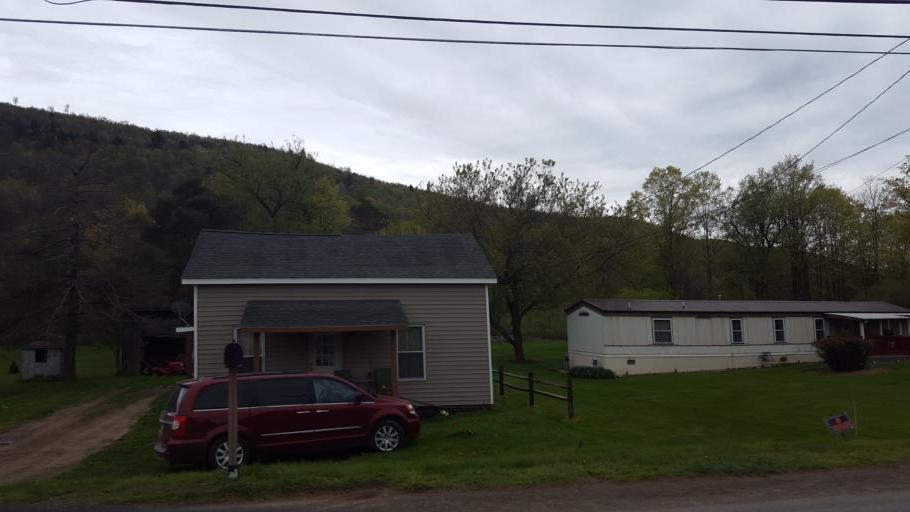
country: US
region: Pennsylvania
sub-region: Tioga County
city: Westfield
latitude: 41.9411
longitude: -77.6487
